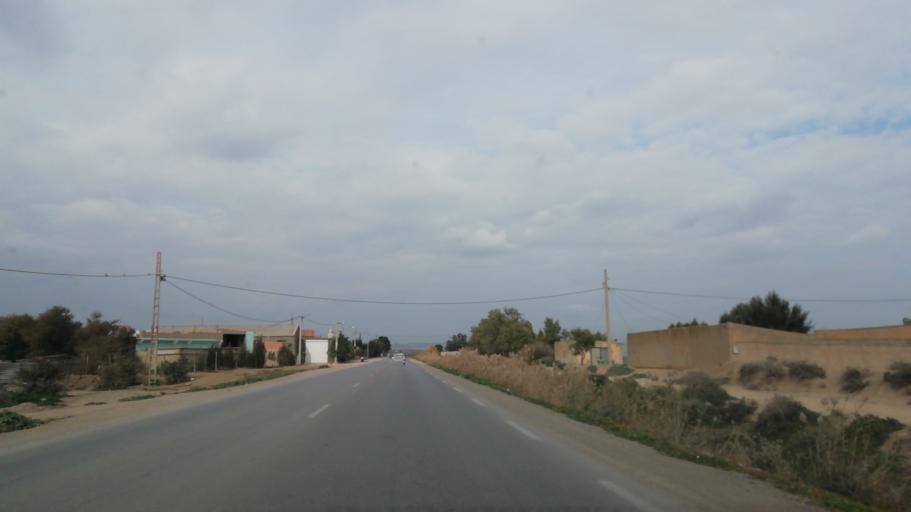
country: DZ
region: Mostaganem
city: Mostaganem
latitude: 35.6957
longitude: 0.0556
